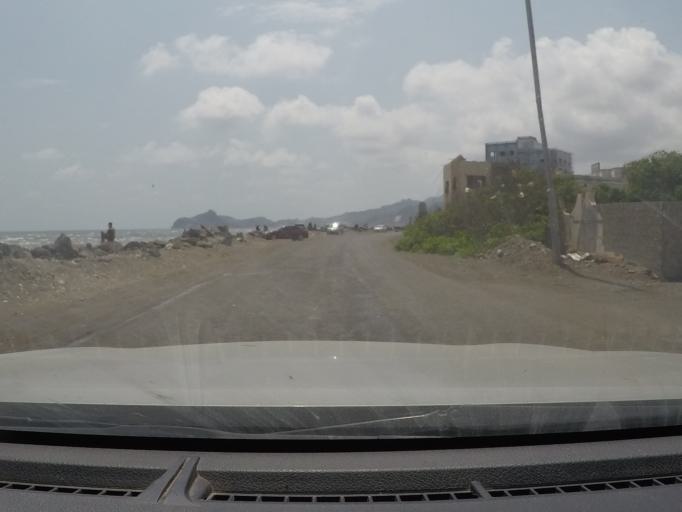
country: YE
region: Aden
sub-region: Khur Maksar
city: Khawr Maksar
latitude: 12.8124
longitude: 45.0437
